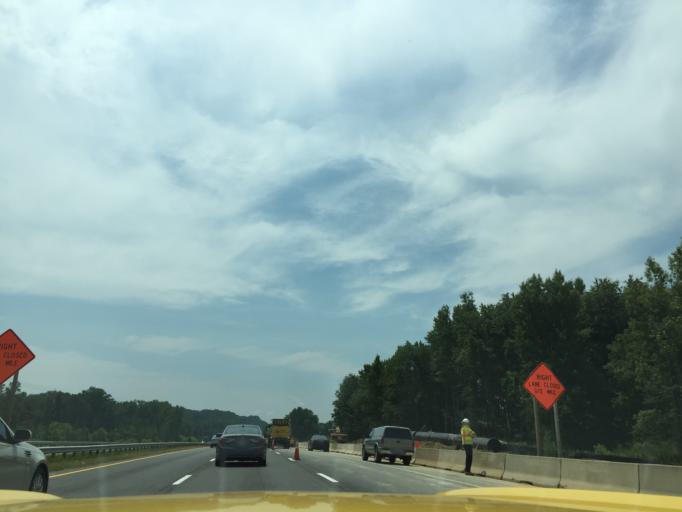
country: US
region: Maryland
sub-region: Prince George's County
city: Friendly
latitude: 38.7329
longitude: -76.9909
